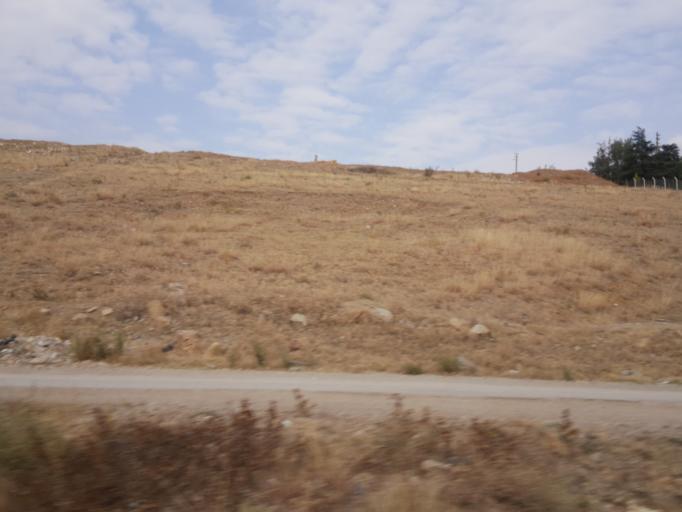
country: TR
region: Kirikkale
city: Bahsili
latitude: 39.8047
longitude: 33.4658
